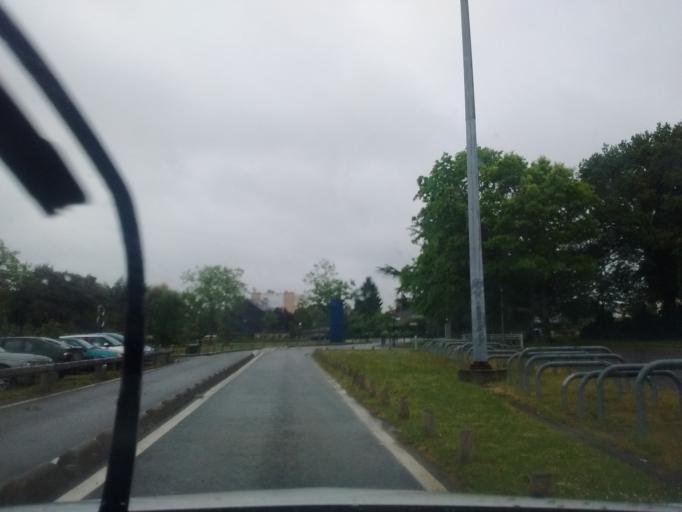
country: FR
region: Pays de la Loire
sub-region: Departement de la Loire-Atlantique
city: Nantes
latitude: 47.2544
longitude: -1.5311
